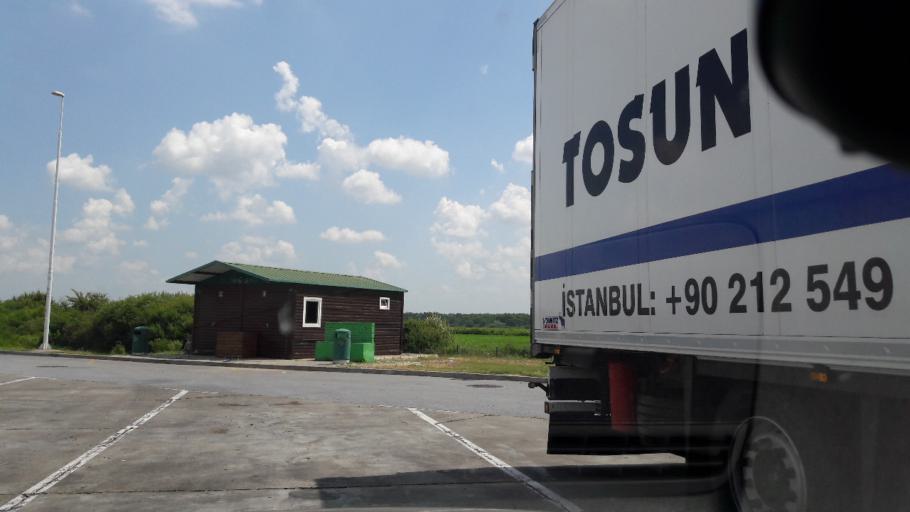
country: RS
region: Autonomna Pokrajina Vojvodina
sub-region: Sremski Okrug
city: Sid
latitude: 45.0476
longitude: 19.1990
